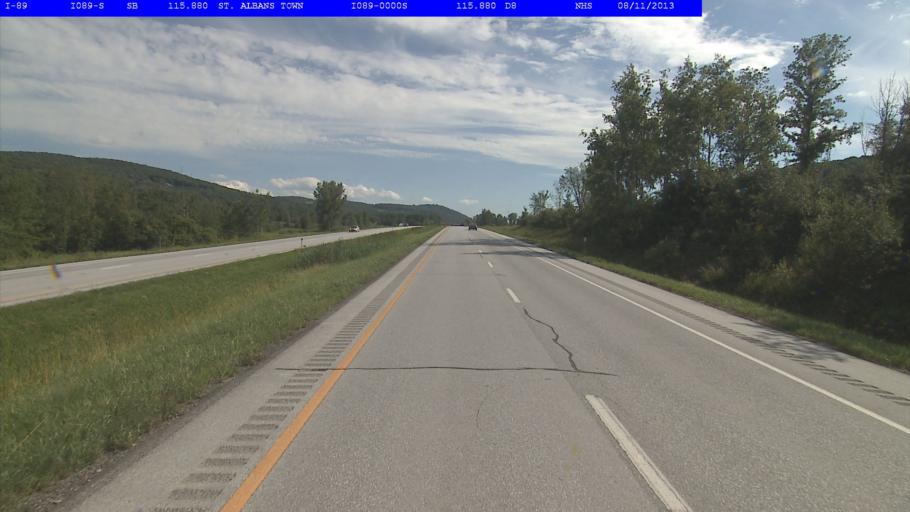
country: US
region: Vermont
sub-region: Franklin County
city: Saint Albans
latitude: 44.8251
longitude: -73.0624
